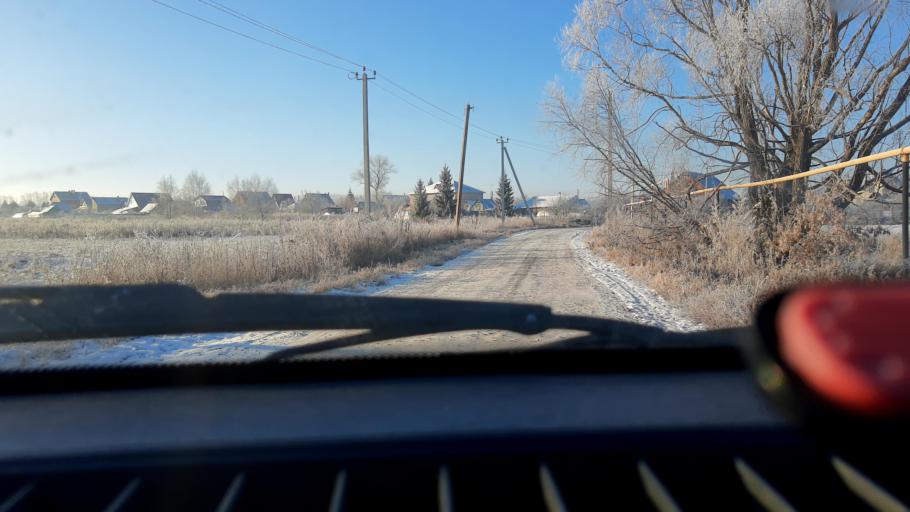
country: RU
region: Bashkortostan
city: Mikhaylovka
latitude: 54.8670
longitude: 55.7613
